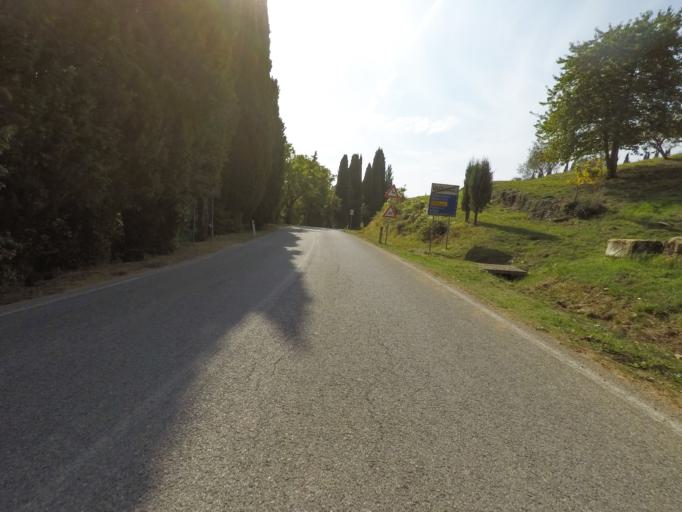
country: IT
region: Tuscany
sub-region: Provincia di Siena
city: Radda in Chianti
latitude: 43.4162
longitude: 11.3488
